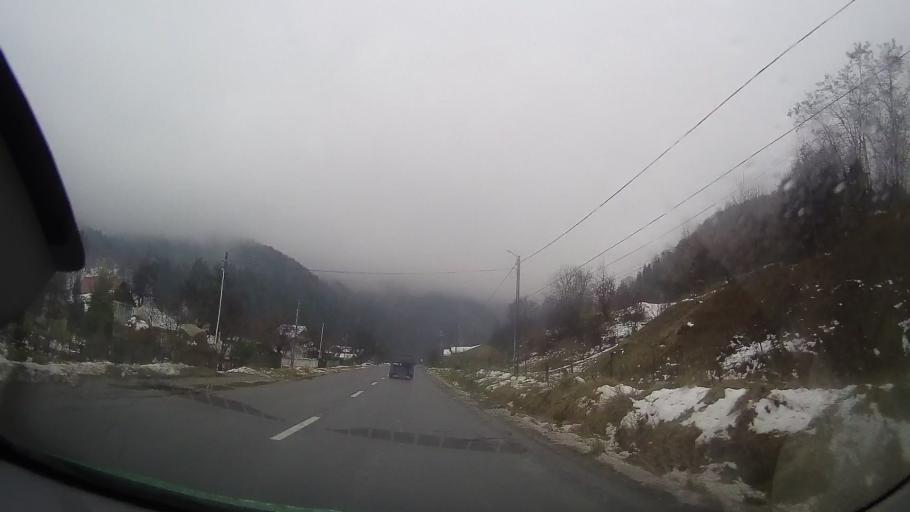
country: RO
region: Neamt
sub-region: Comuna Pangarati
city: Stejaru
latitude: 46.8957
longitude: 26.1700
